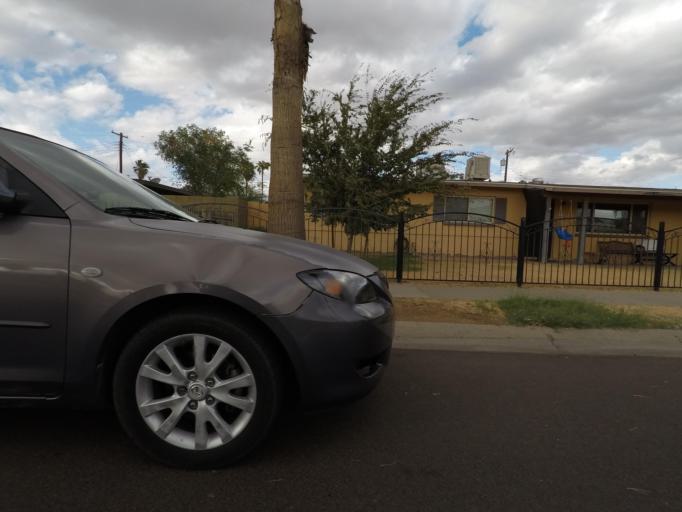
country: US
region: Arizona
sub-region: Maricopa County
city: Glendale
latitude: 33.5035
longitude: -112.1403
